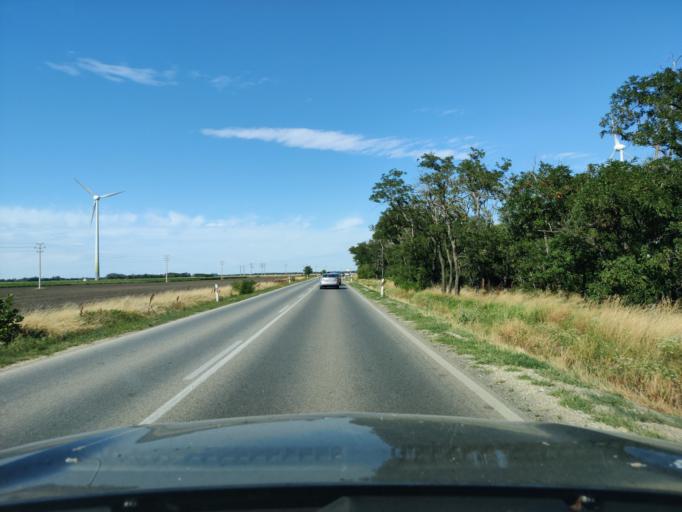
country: HU
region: Gyor-Moson-Sopron
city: Janossomorja
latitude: 47.8116
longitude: 17.1738
